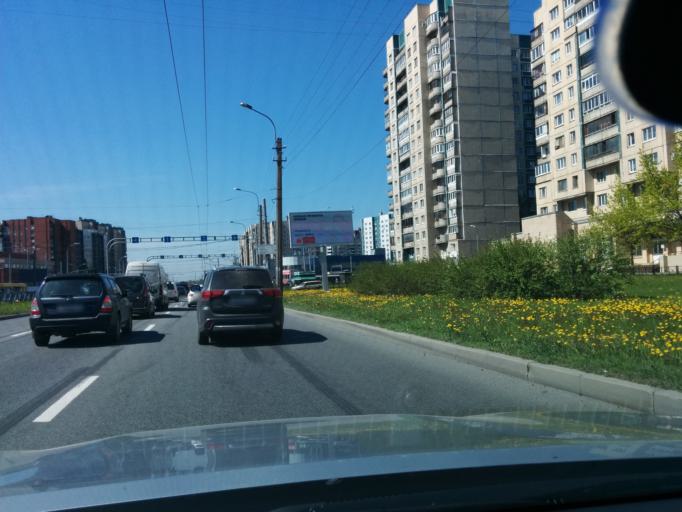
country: RU
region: St.-Petersburg
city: Krasnogvargeisky
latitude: 59.9454
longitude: 30.4943
